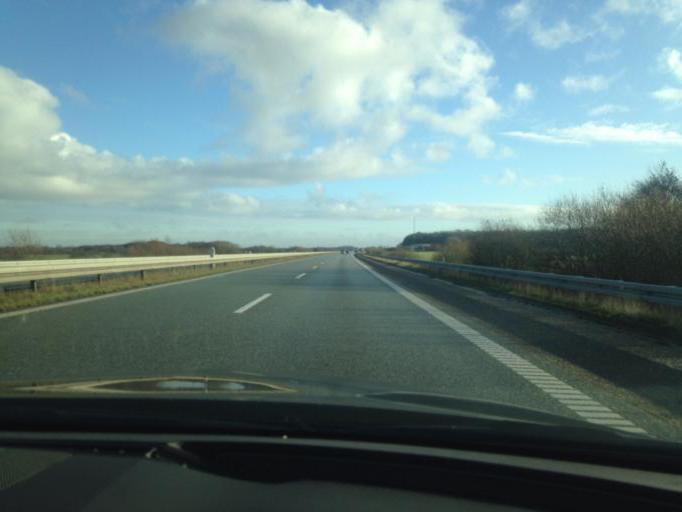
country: DK
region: South Denmark
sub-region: Vejen Kommune
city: Brorup
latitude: 55.5015
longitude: 9.0602
